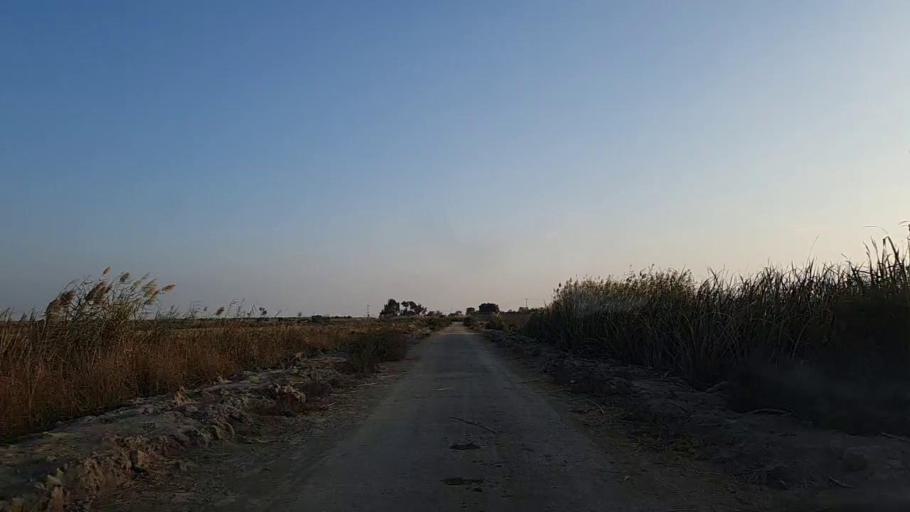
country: PK
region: Sindh
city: Sanghar
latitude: 26.2594
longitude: 68.9778
